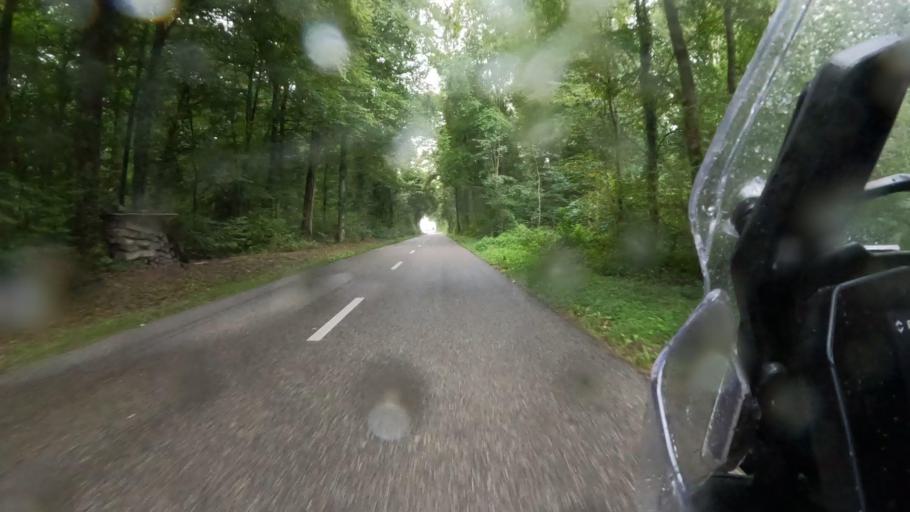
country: CH
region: Zurich
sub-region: Bezirk Andelfingen
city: Marthalen
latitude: 47.6403
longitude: 8.6499
